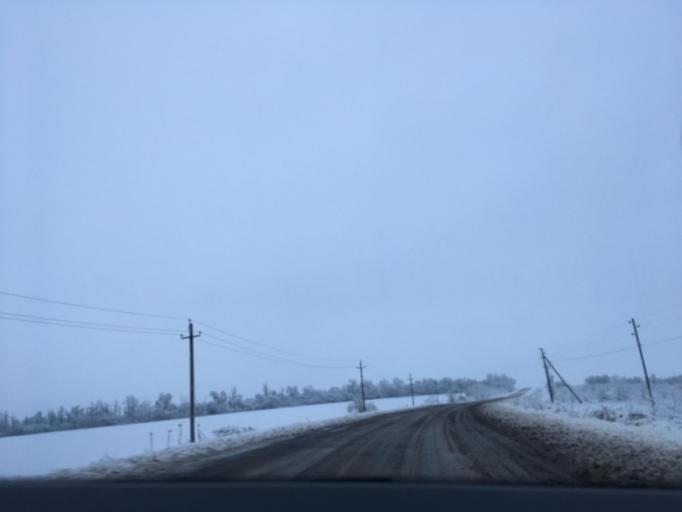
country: RU
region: Voronezj
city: Verkhniy Mamon
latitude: 50.0339
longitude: 40.0615
